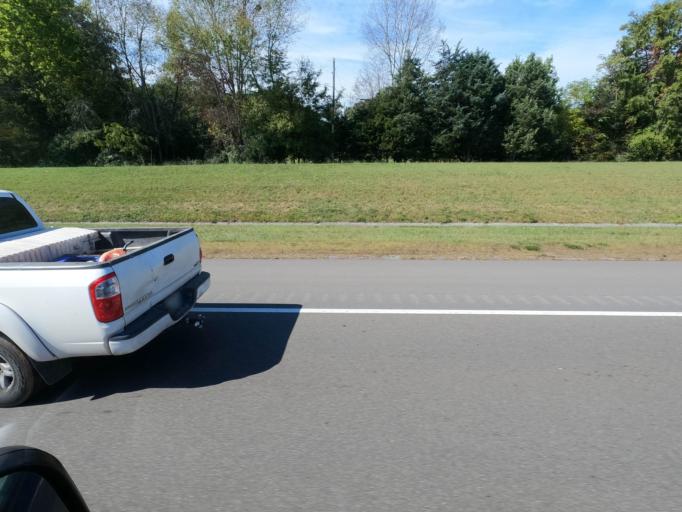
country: US
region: Tennessee
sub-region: Hamblen County
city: Morristown
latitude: 36.2753
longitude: -83.2822
